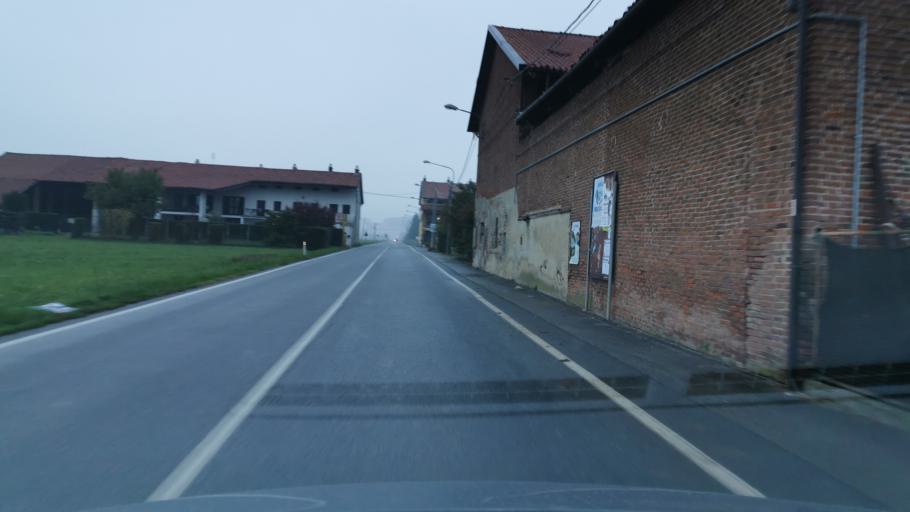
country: IT
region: Piedmont
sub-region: Provincia di Torino
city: Ciconio
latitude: 45.3472
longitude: 7.7660
